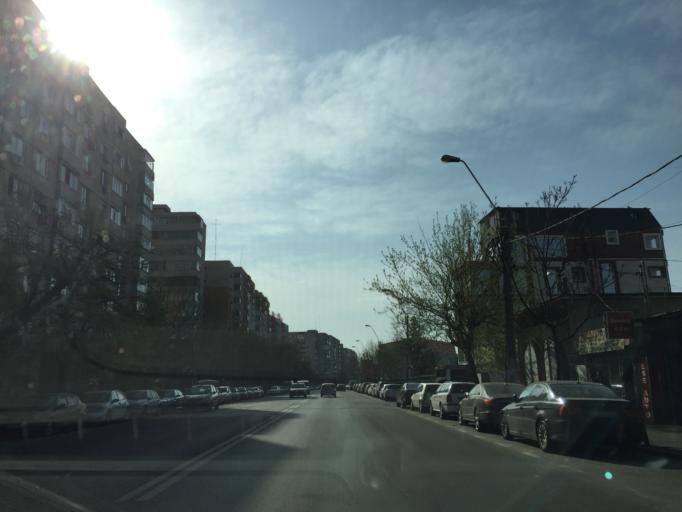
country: RO
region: Bucuresti
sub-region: Municipiul Bucuresti
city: Bucharest
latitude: 44.4132
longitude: 26.1338
